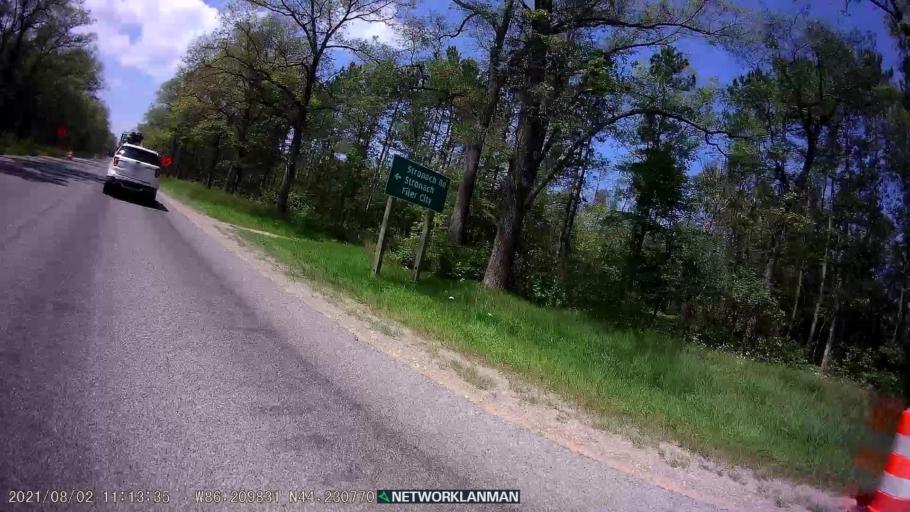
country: US
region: Michigan
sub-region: Manistee County
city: Manistee
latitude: 44.2308
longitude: -86.2099
